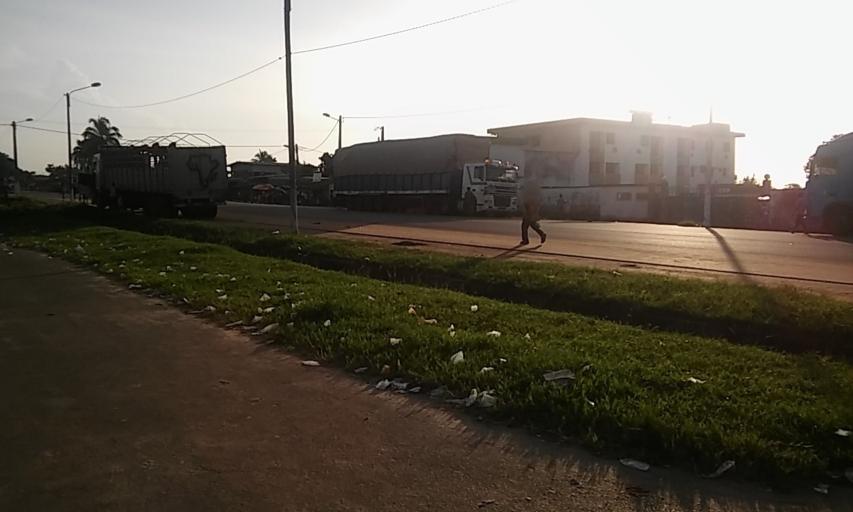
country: CI
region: Dix-Huit Montagnes
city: Duekoue
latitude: 6.7422
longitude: -7.3443
